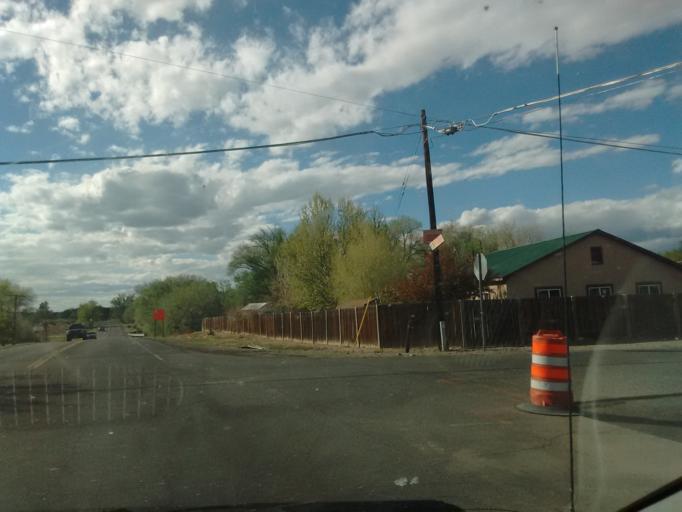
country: US
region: Colorado
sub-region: Mesa County
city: Redlands
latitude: 39.0716
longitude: -108.6190
